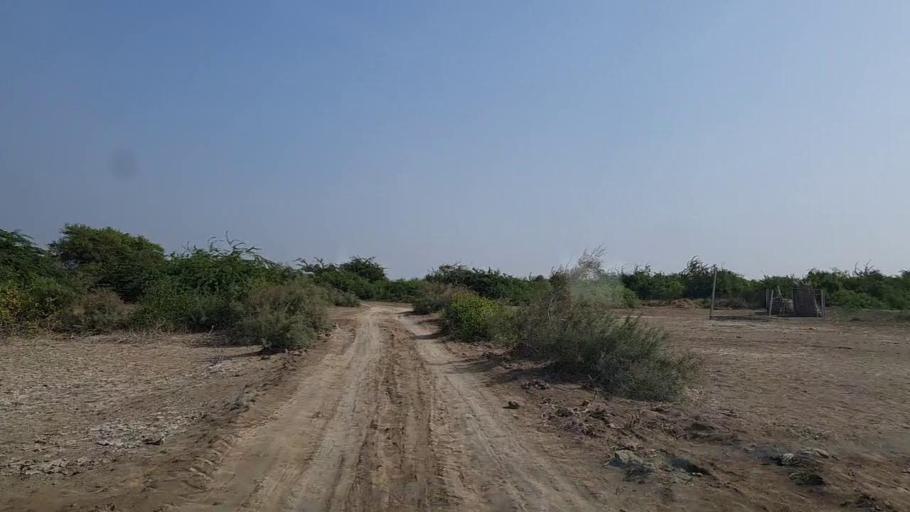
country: PK
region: Sindh
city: Mirpur Sakro
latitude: 24.5524
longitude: 67.5581
